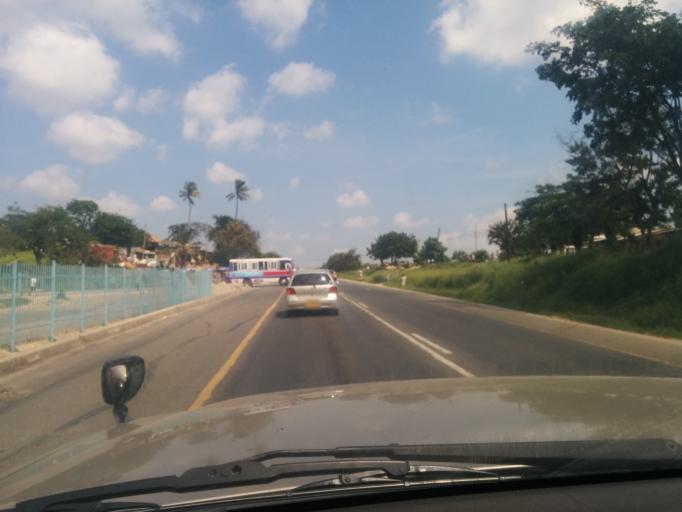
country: TZ
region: Pwani
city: Kisarawe
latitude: -6.7860
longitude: 39.1116
